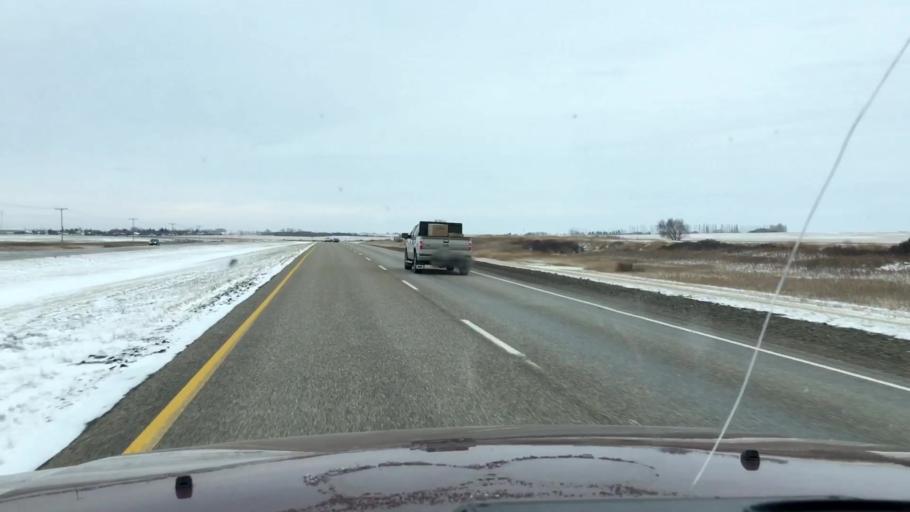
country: CA
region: Saskatchewan
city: Moose Jaw
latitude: 50.9561
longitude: -105.7111
